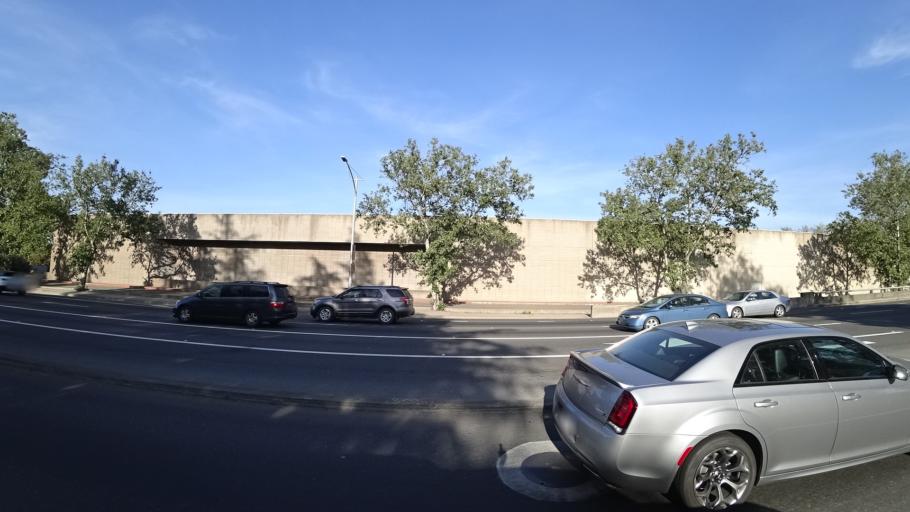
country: US
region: California
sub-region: Yuba County
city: Marysville
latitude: 39.1370
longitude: -121.5902
